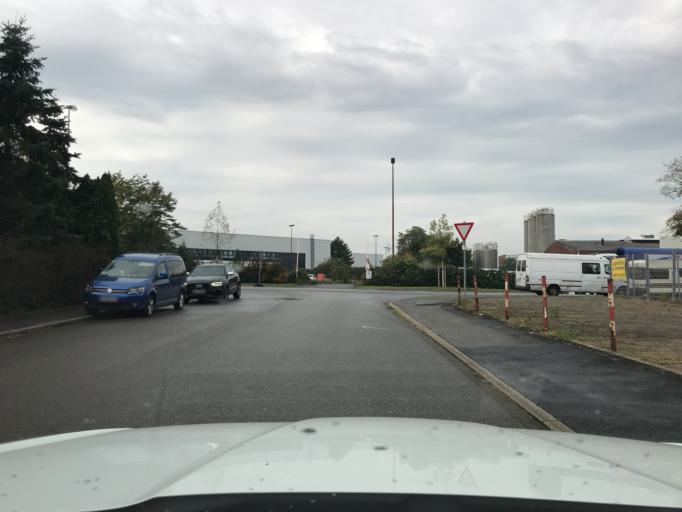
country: DE
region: North Rhine-Westphalia
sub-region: Regierungsbezirk Dusseldorf
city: Muelheim (Ruhr)
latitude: 51.4328
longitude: 6.8561
